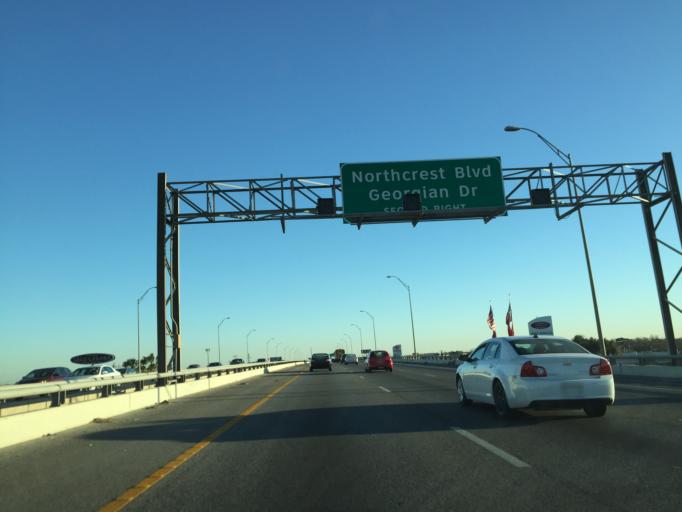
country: US
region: Texas
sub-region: Travis County
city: Wells Branch
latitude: 30.3597
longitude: -97.7166
